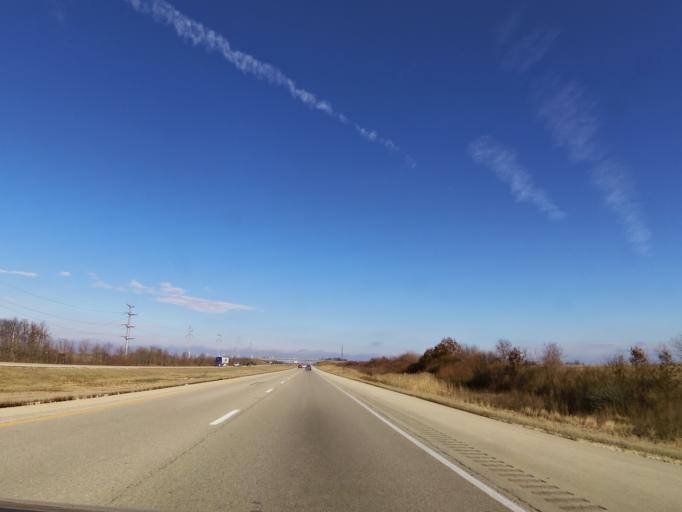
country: US
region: Illinois
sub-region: LaSalle County
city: Mendota
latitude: 41.6648
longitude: -89.0584
